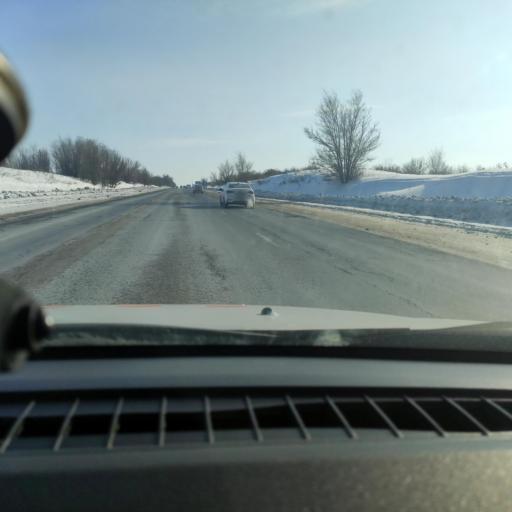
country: RU
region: Samara
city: Smyshlyayevka
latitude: 53.2751
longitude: 50.4645
